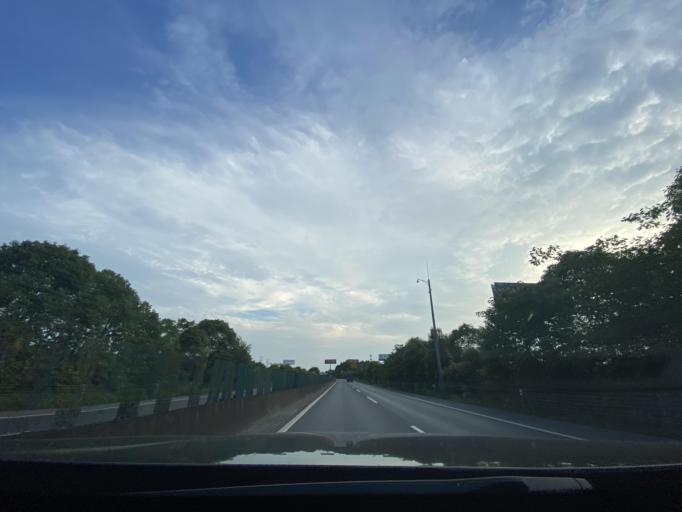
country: CN
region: Sichuan
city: Luojiang
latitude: 31.3644
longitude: 104.5354
